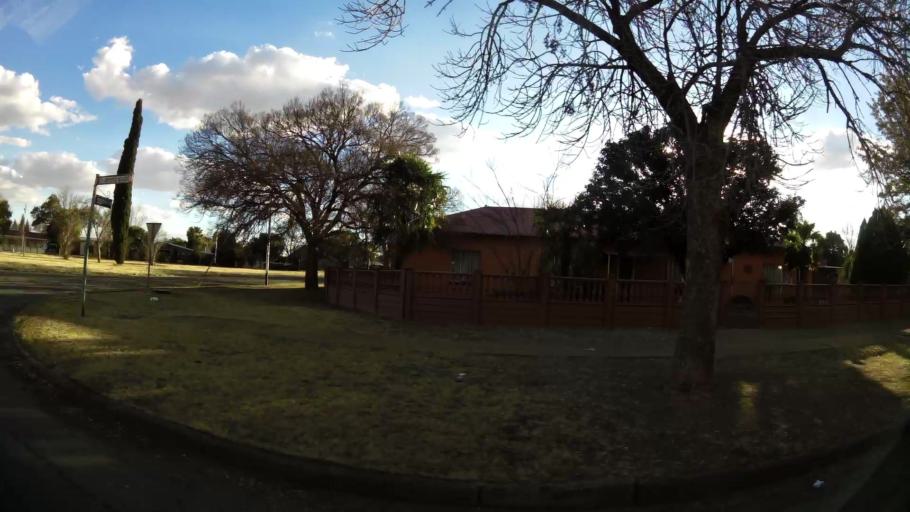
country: ZA
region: North-West
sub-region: Dr Kenneth Kaunda District Municipality
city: Potchefstroom
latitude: -26.7404
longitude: 27.0887
